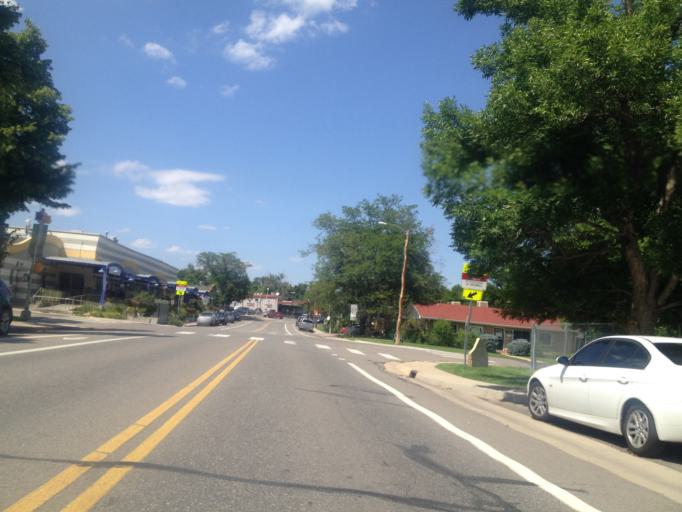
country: US
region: Colorado
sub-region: Boulder County
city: Boulder
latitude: 40.0241
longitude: -105.2806
